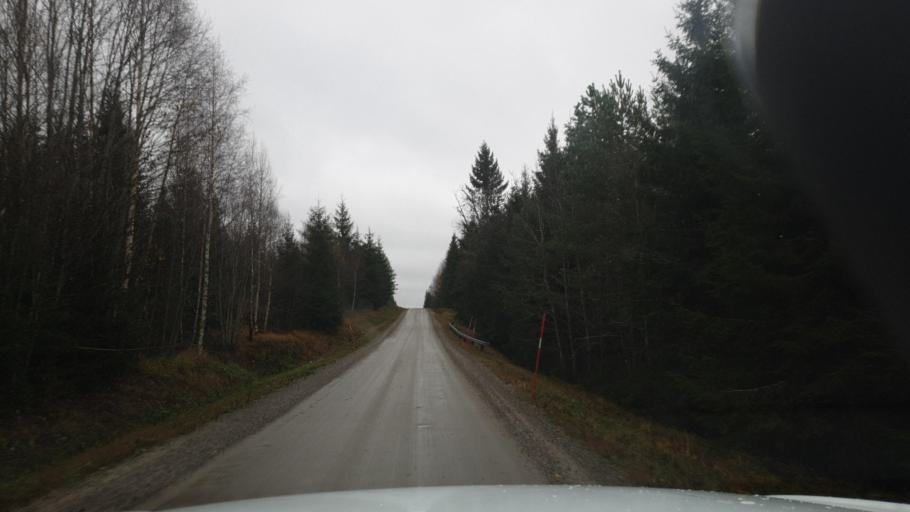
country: SE
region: Vaermland
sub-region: Arvika Kommun
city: Arvika
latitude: 59.8508
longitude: 12.7197
